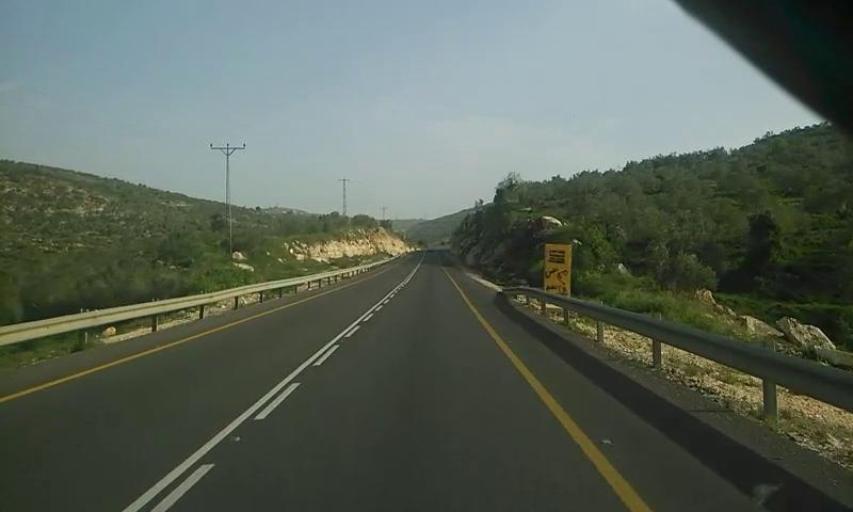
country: PS
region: West Bank
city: Jit
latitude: 32.2224
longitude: 35.1741
